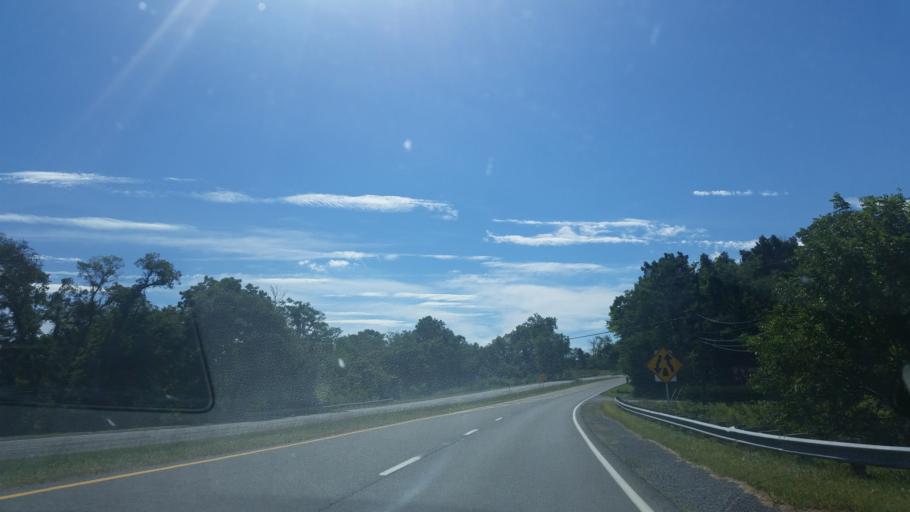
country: US
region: Virginia
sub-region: City of Winchester
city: Winchester
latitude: 39.2039
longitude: -78.1655
